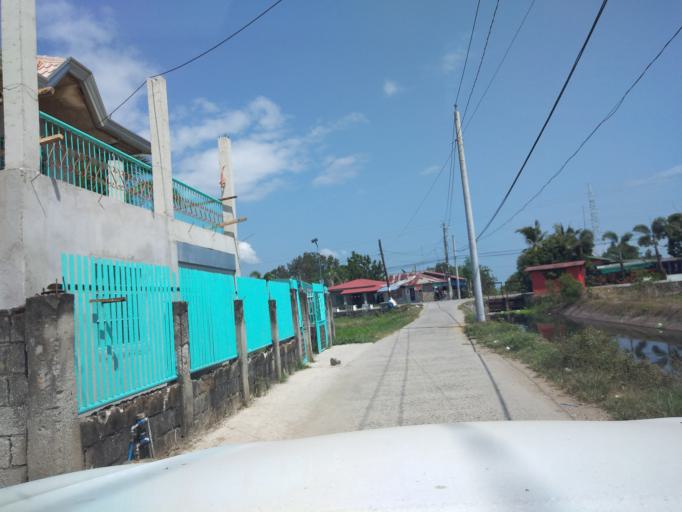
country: PH
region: Central Luzon
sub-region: Province of Pampanga
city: Talang
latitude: 15.0252
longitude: 120.8381
